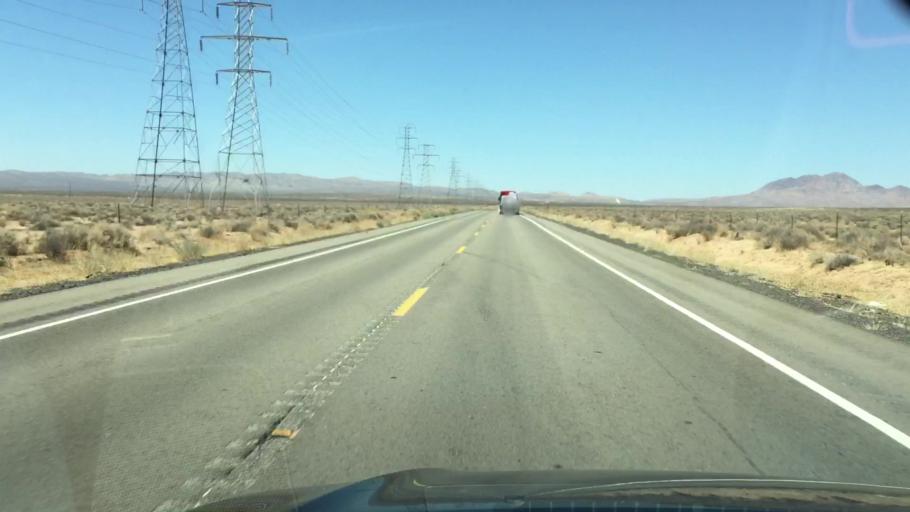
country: US
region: California
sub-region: Kern County
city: Boron
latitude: 35.2077
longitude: -117.6016
